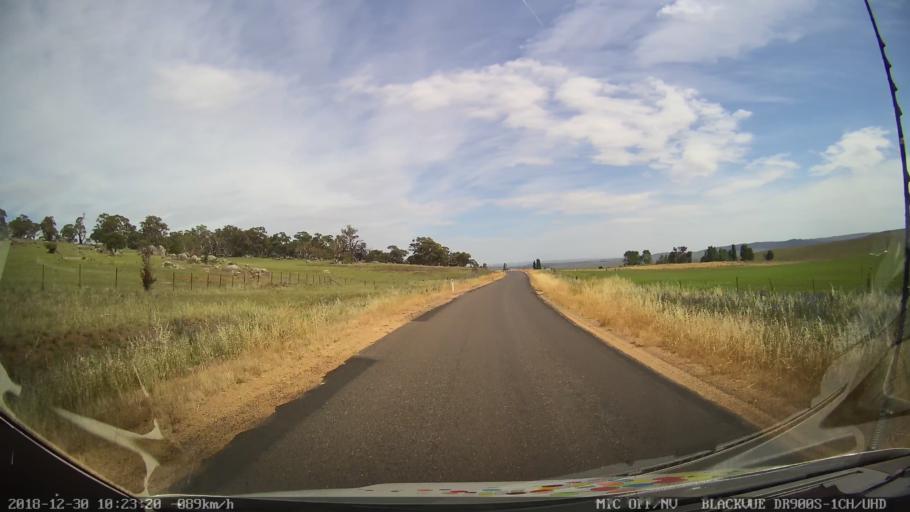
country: AU
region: New South Wales
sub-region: Snowy River
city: Berridale
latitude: -36.5388
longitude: 148.9828
